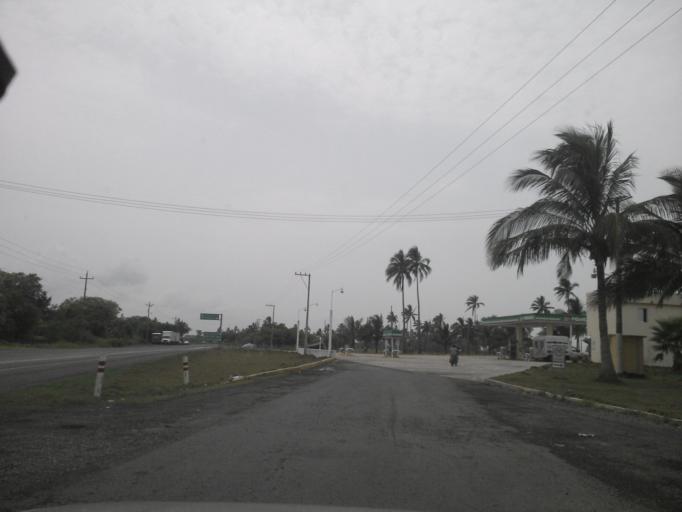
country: MX
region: Veracruz
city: Tecolutla
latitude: 20.3787
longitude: -96.9279
